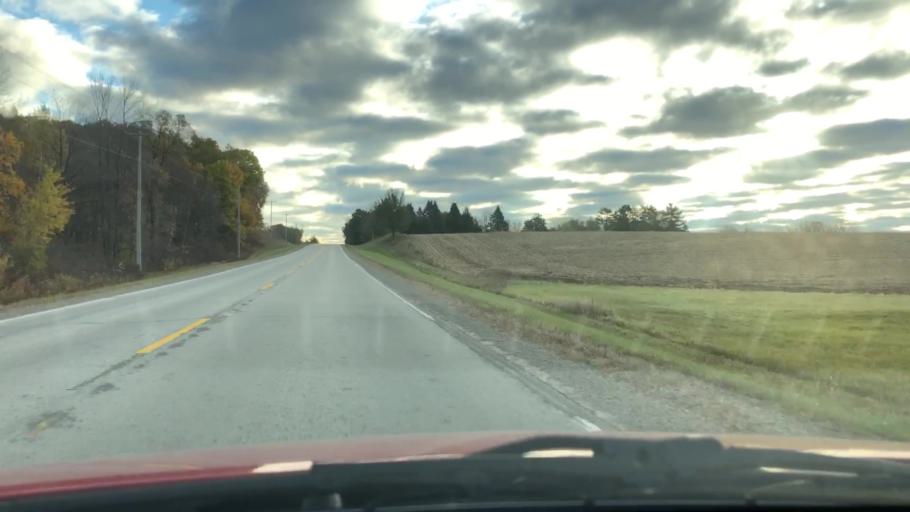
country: US
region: Wisconsin
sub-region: Outagamie County
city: Seymour
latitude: 44.4440
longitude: -88.2704
